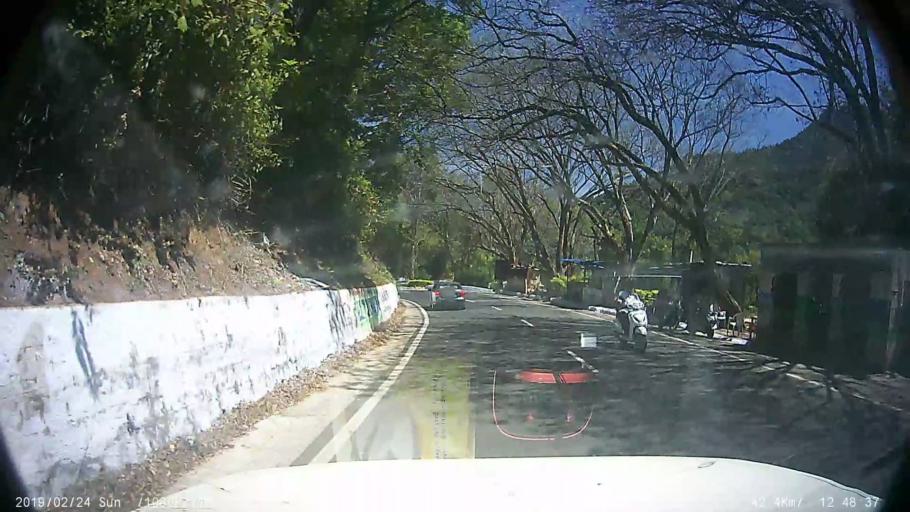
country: IN
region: Tamil Nadu
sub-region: Nilgiri
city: Wellington
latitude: 11.3299
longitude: 76.8020
